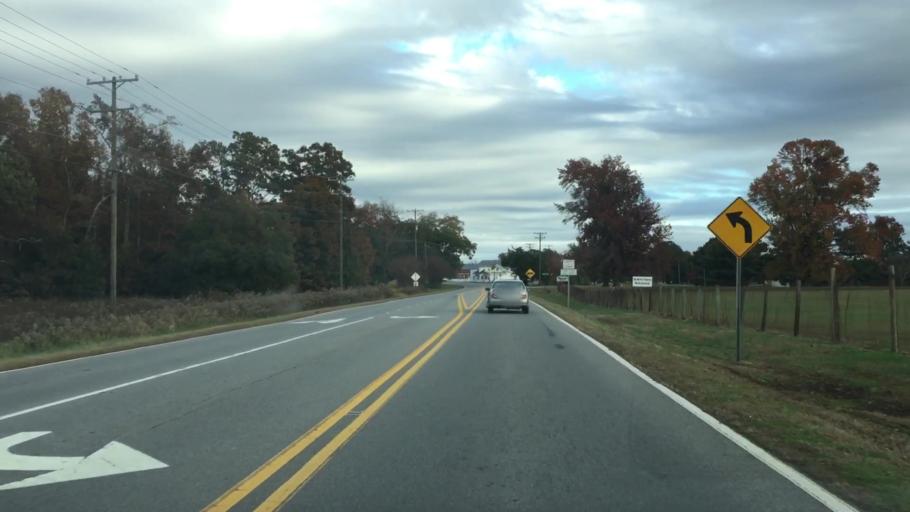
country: US
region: North Carolina
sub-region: Rockingham County
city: Reidsville
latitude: 36.2897
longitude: -79.7345
